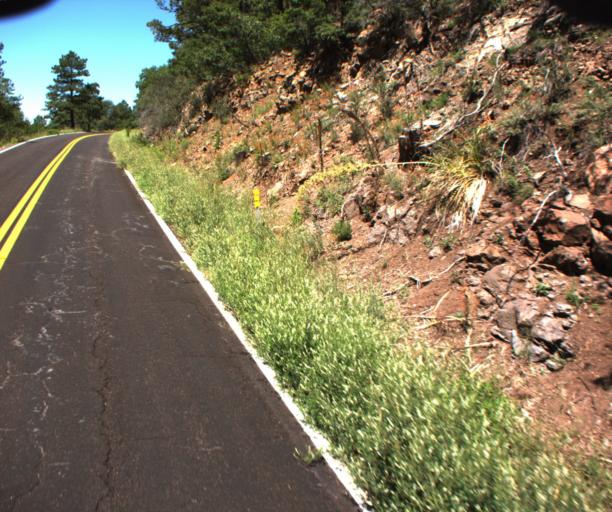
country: US
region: Arizona
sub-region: Greenlee County
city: Morenci
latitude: 33.4482
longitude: -109.3625
